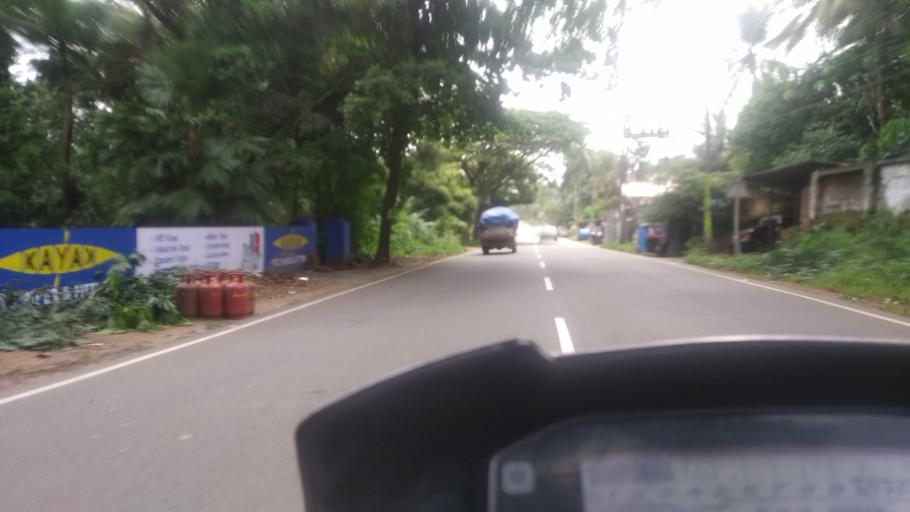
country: IN
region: Kerala
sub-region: Ernakulam
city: Aluva
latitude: 10.1264
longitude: 76.3289
